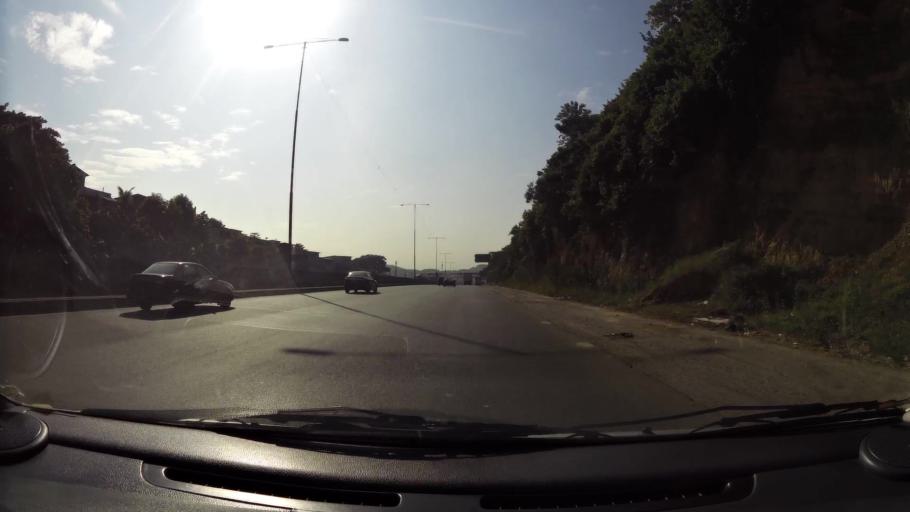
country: EC
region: Guayas
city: Eloy Alfaro
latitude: -2.0790
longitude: -79.9307
